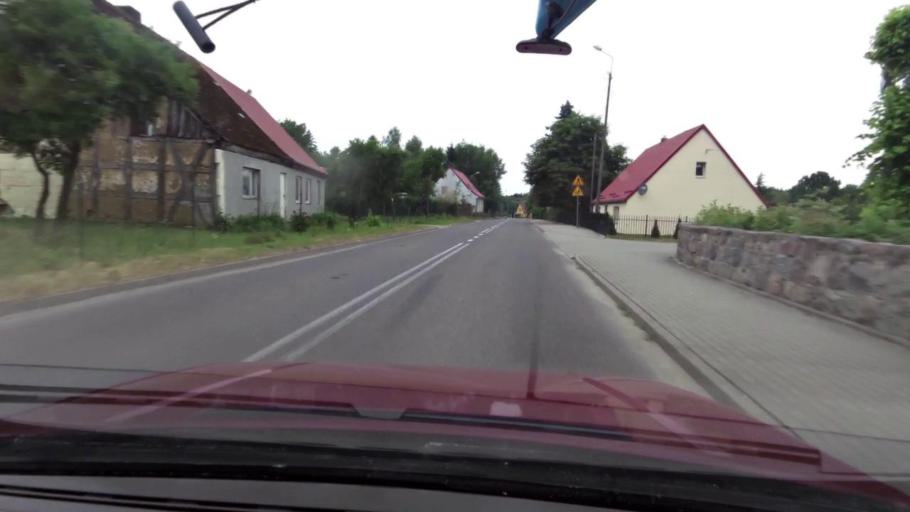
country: PL
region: West Pomeranian Voivodeship
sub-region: Powiat koszalinski
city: Sianow
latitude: 54.1801
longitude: 16.3827
